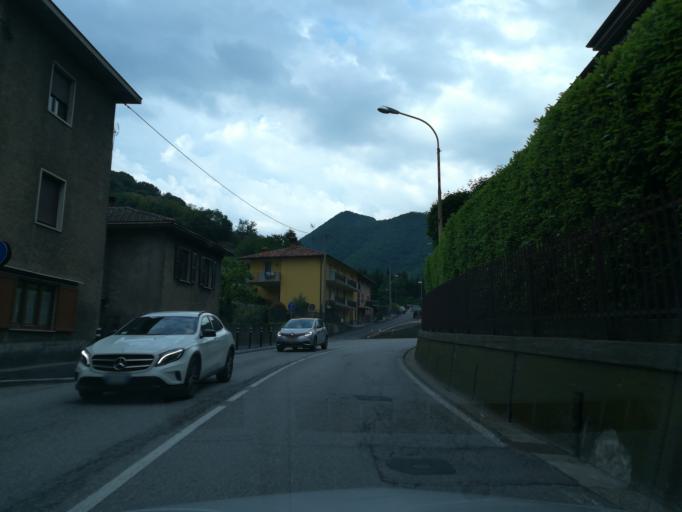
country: IT
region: Lombardy
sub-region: Provincia di Bergamo
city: Almenno San Salvatore
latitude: 45.7552
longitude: 9.5959
